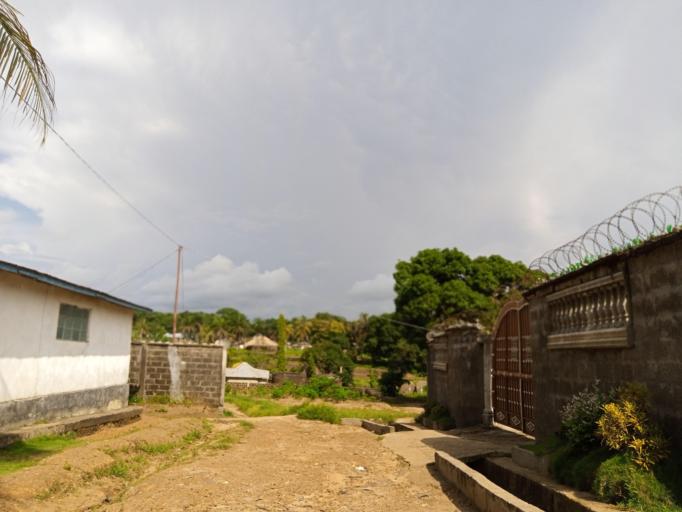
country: SL
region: Northern Province
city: Masoyila
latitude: 8.6071
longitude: -13.2026
